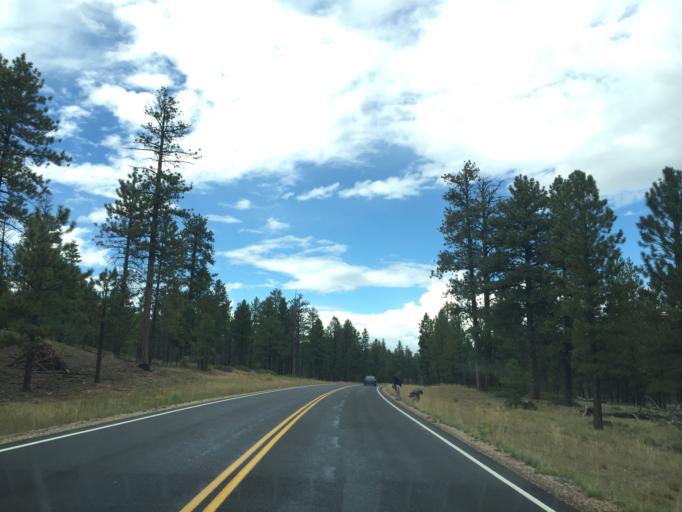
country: US
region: Utah
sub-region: Garfield County
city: Panguitch
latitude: 37.6298
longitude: -112.1734
